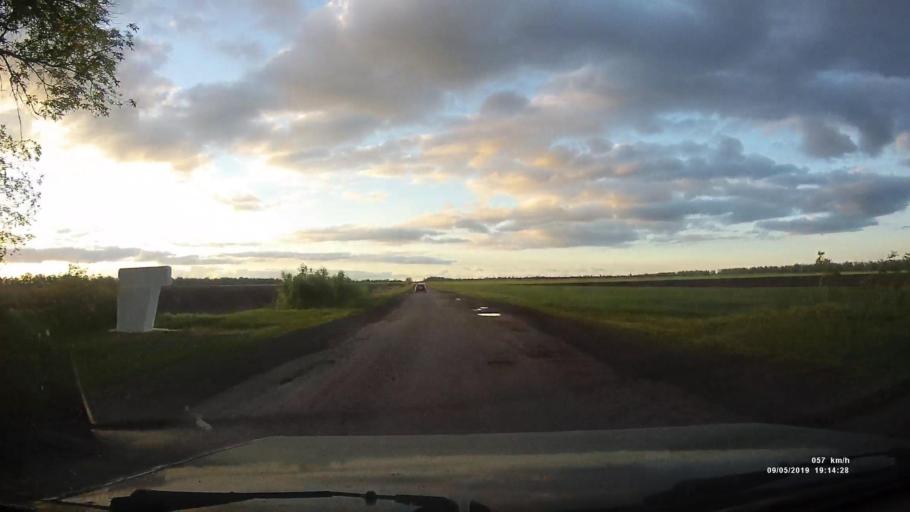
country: RU
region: Krasnodarskiy
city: Kanelovskaya
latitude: 46.7595
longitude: 39.2142
